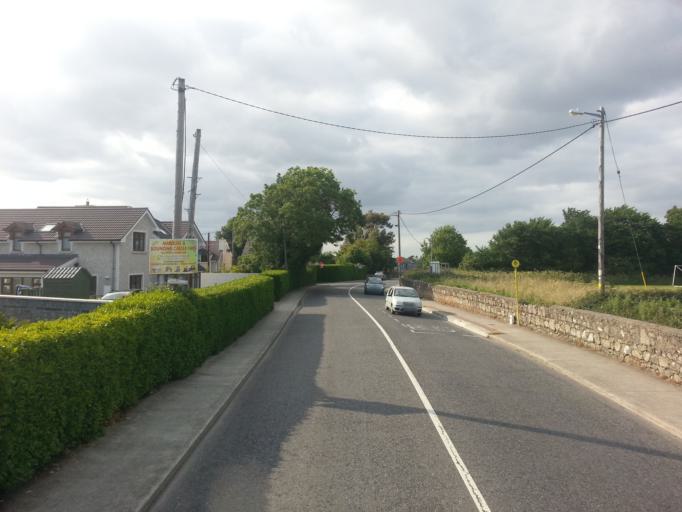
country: IE
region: Leinster
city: Foxrock
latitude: 53.2376
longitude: -6.1953
